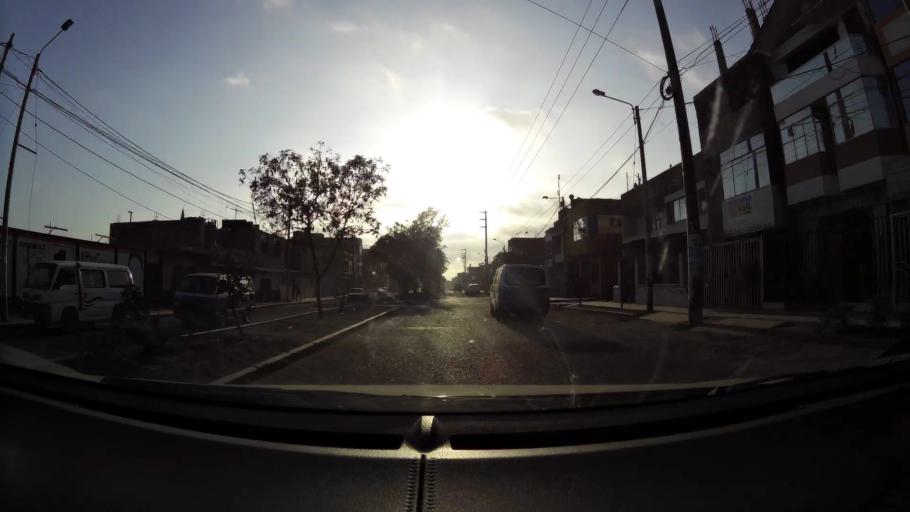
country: PE
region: La Libertad
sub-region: Provincia de Trujillo
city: El Porvenir
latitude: -8.0888
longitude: -78.9950
